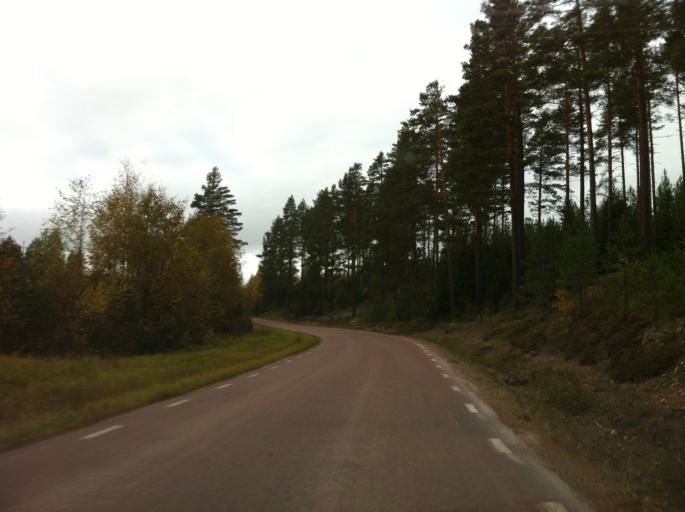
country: SE
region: Dalarna
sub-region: Mora Kommun
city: Mora
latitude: 61.0860
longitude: 14.3839
